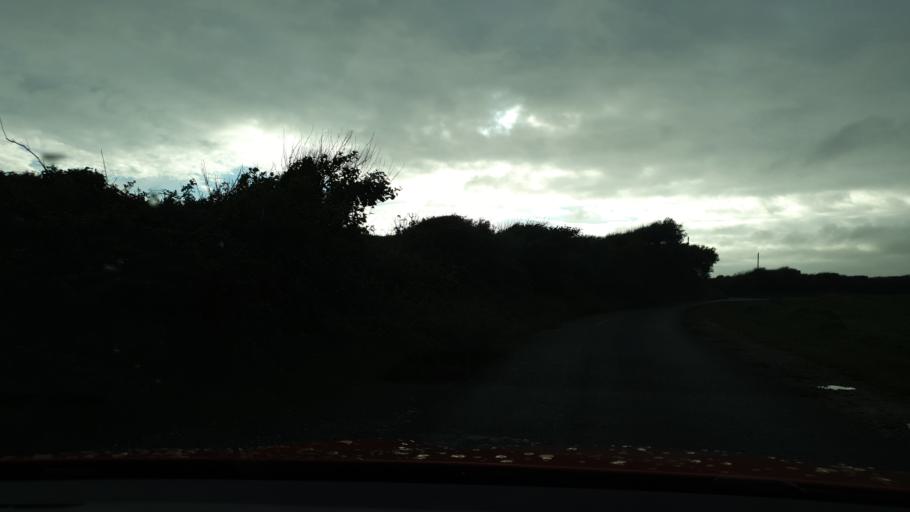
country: GB
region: England
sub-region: Cumbria
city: Barrow in Furness
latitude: 54.0656
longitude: -3.2219
